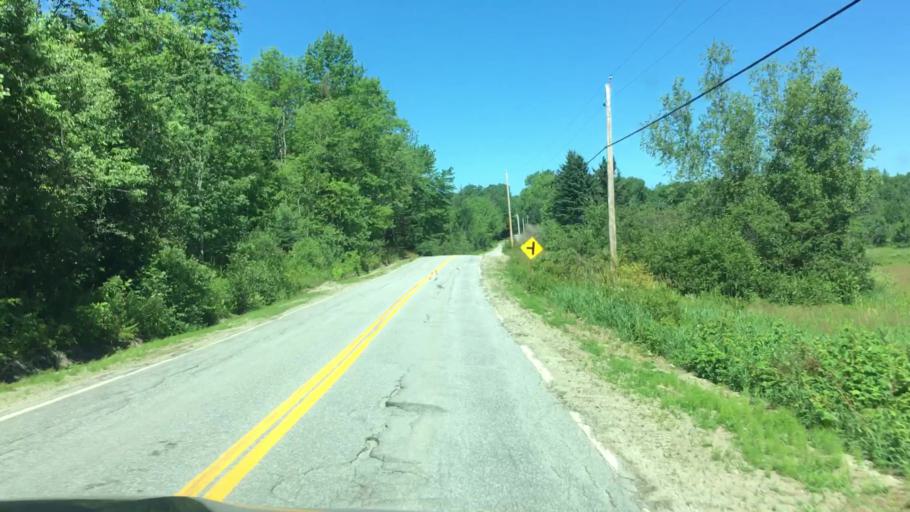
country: US
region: Maine
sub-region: Hancock County
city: Penobscot
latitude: 44.4249
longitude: -68.7087
